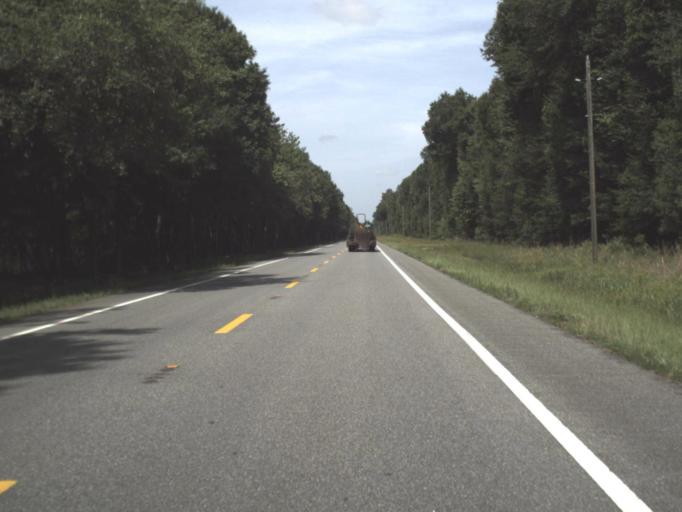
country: US
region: Florida
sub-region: Lafayette County
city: Mayo
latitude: 29.9662
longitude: -83.2245
